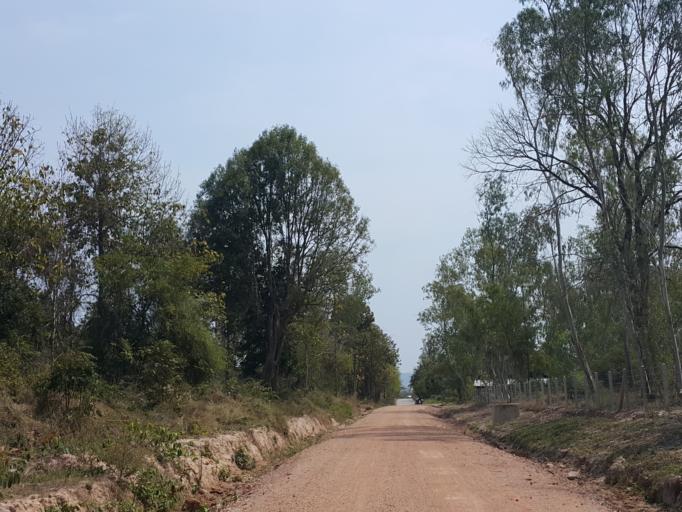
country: TH
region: Lampang
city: Lampang
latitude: 18.3076
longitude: 99.4208
